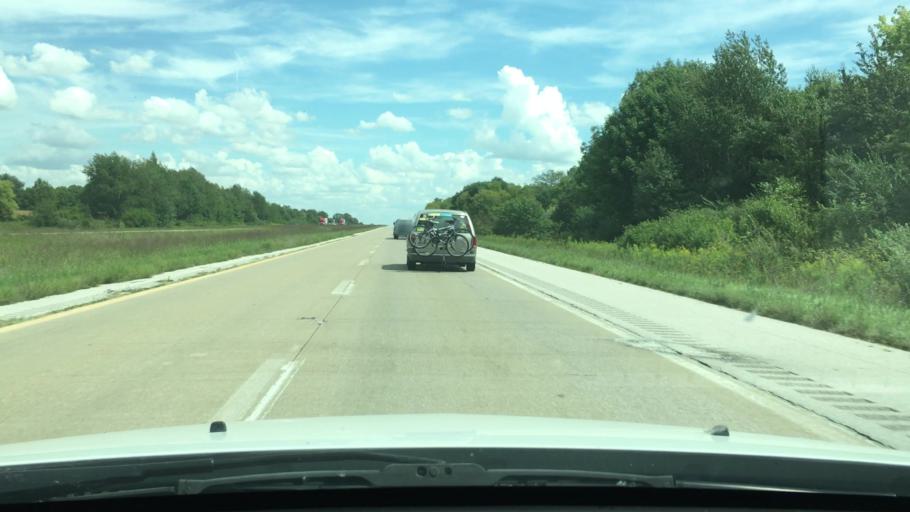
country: US
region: Illinois
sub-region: Scott County
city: Winchester
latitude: 39.6809
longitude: -90.4974
